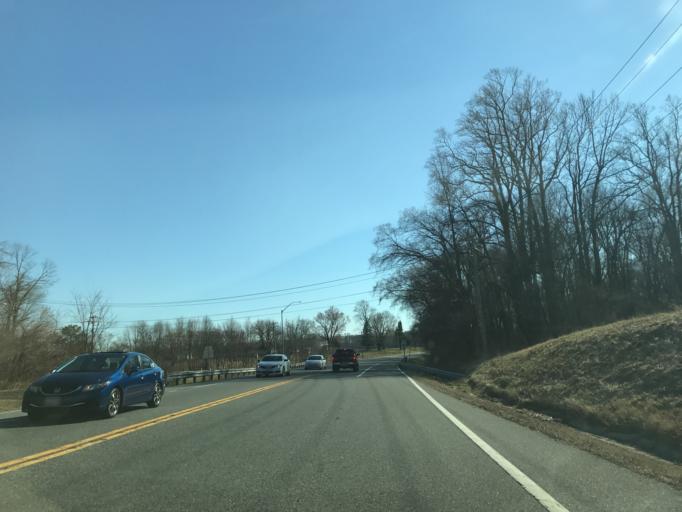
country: US
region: Maryland
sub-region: Queen Anne's County
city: Centreville
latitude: 39.0015
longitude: -76.0734
